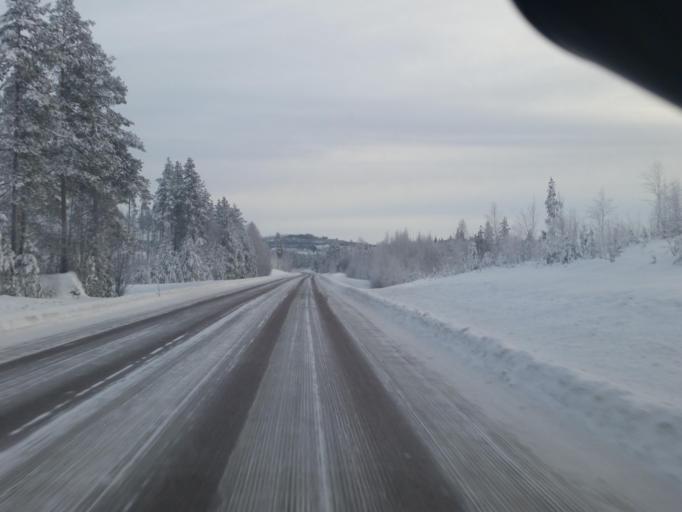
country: SE
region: Norrbotten
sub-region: Alvsbyns Kommun
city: AElvsbyn
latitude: 65.6727
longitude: 21.1380
